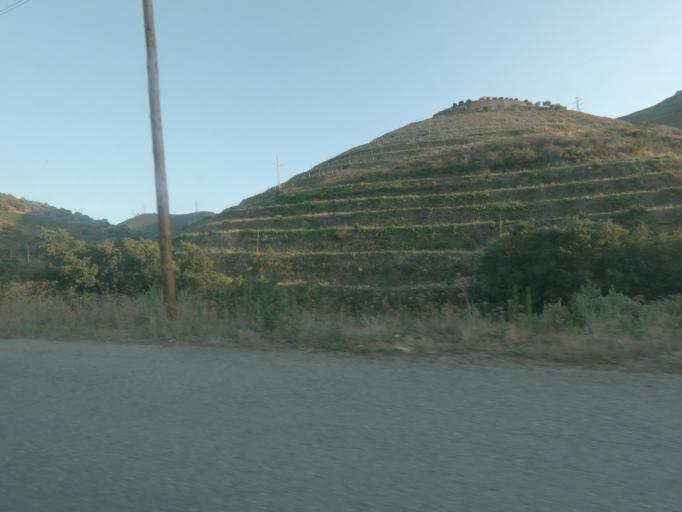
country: PT
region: Viseu
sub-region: Armamar
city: Armamar
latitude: 41.1378
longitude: -7.6938
